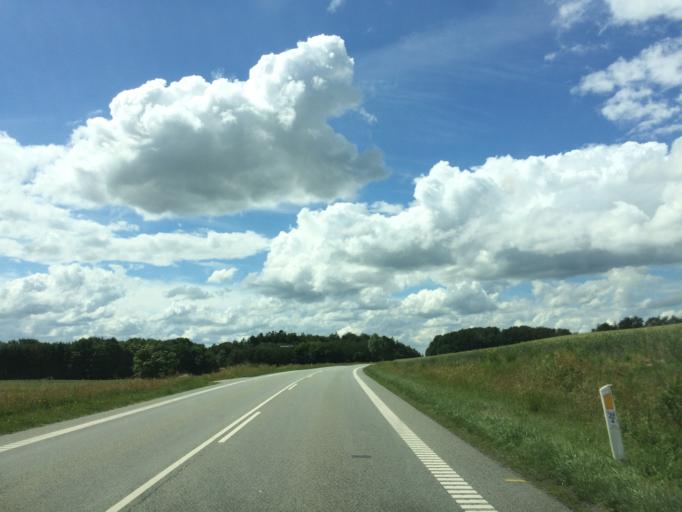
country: DK
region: North Denmark
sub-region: Mariagerfjord Kommune
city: Hobro
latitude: 56.6153
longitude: 9.7078
